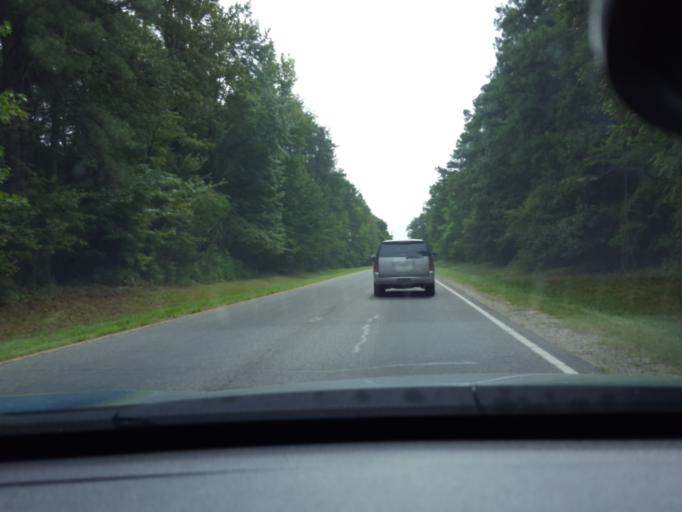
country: US
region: Virginia
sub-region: Caroline County
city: Bowling Green
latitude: 38.1137
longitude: -77.2613
